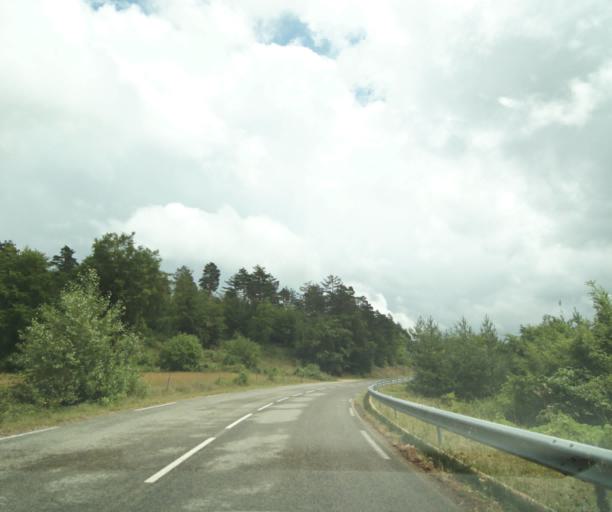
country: FR
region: Languedoc-Roussillon
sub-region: Departement de la Lozere
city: La Canourgue
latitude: 44.4094
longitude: 3.1658
